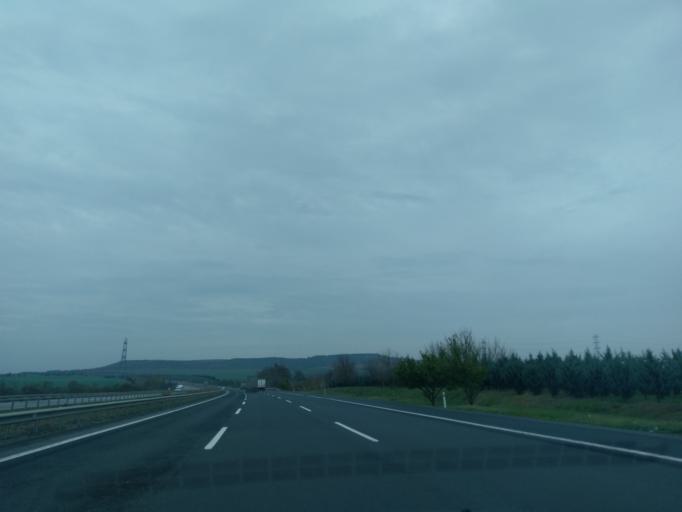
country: TR
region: Istanbul
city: Canta
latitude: 41.1498
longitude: 28.1456
